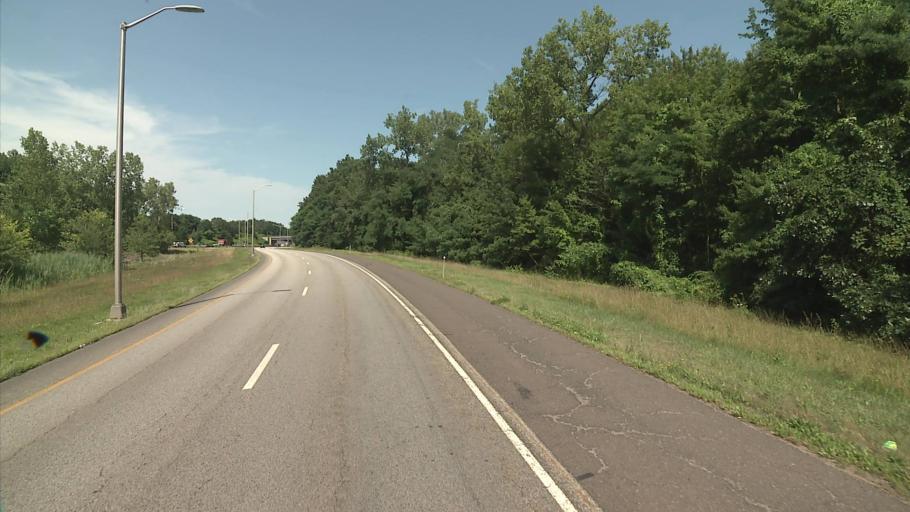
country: US
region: Connecticut
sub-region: Hartford County
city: Windsor Locks
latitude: 41.9007
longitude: -72.6364
